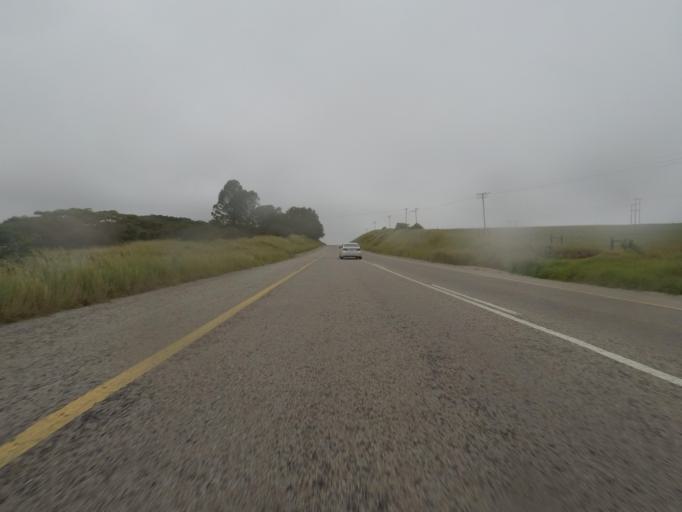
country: ZA
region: Eastern Cape
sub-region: Cacadu District Municipality
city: Grahamstown
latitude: -33.6446
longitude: 26.3778
